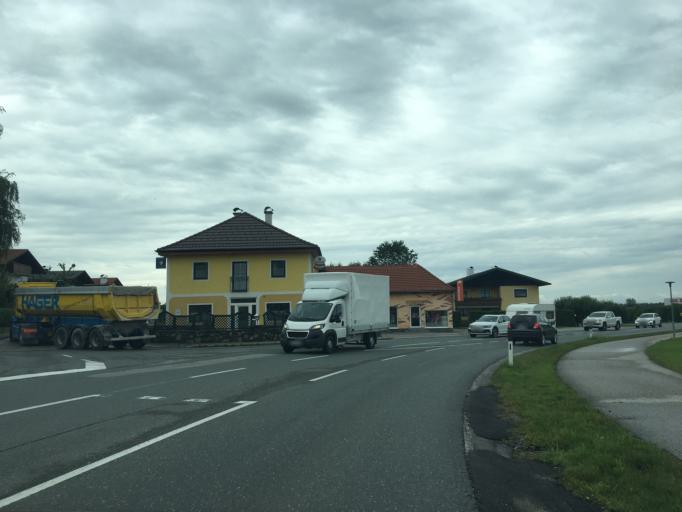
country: AT
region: Salzburg
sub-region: Politischer Bezirk Salzburg-Umgebung
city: Lamprechtshausen
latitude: 47.9978
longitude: 12.9560
